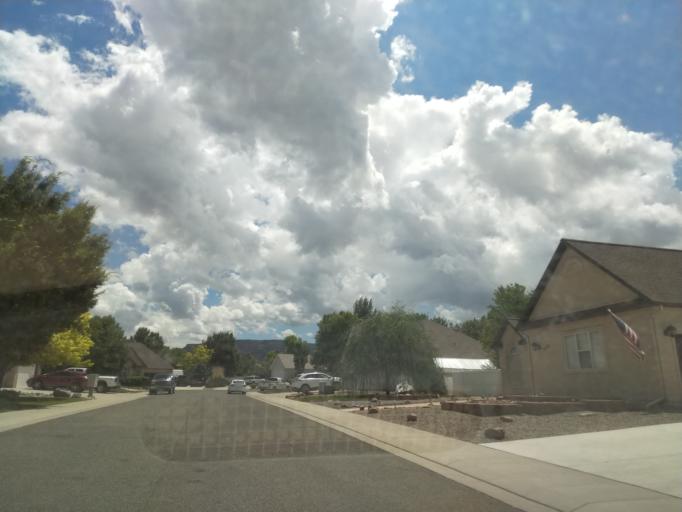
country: US
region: Colorado
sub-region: Mesa County
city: Redlands
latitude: 39.0720
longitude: -108.6463
